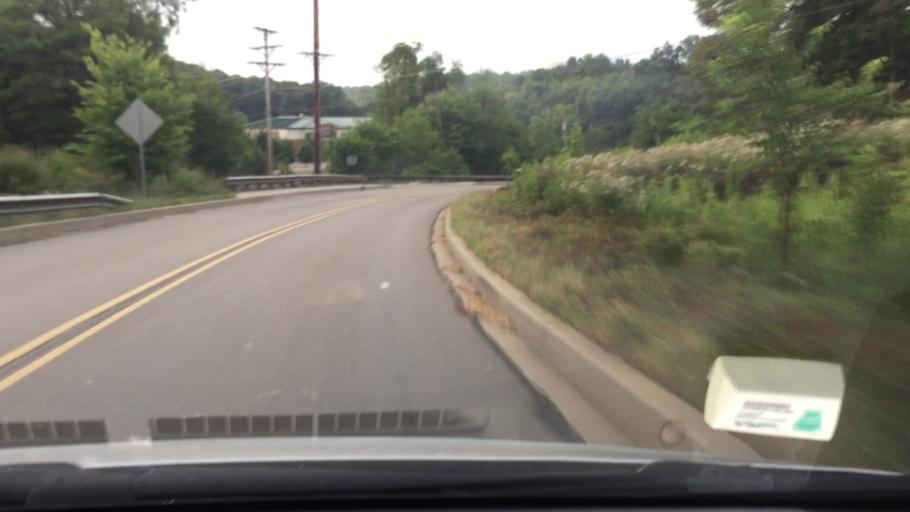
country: US
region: Pennsylvania
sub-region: Allegheny County
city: Bradford Woods
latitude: 40.6292
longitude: -80.0544
